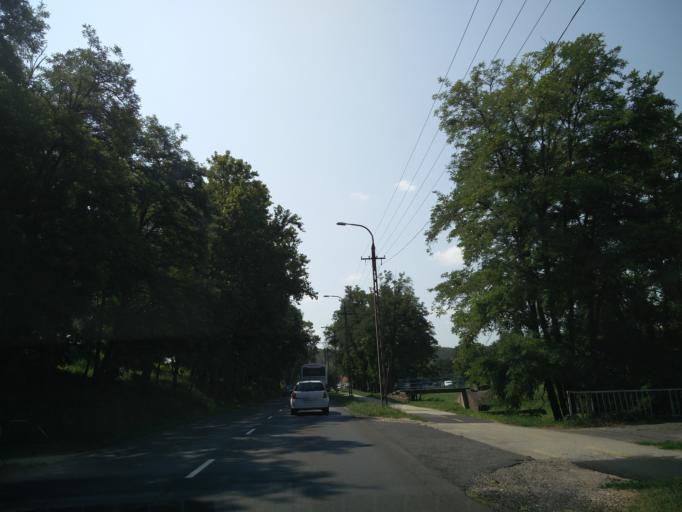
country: HU
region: Zala
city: Zalaegerszeg
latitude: 46.8259
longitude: 16.8282
